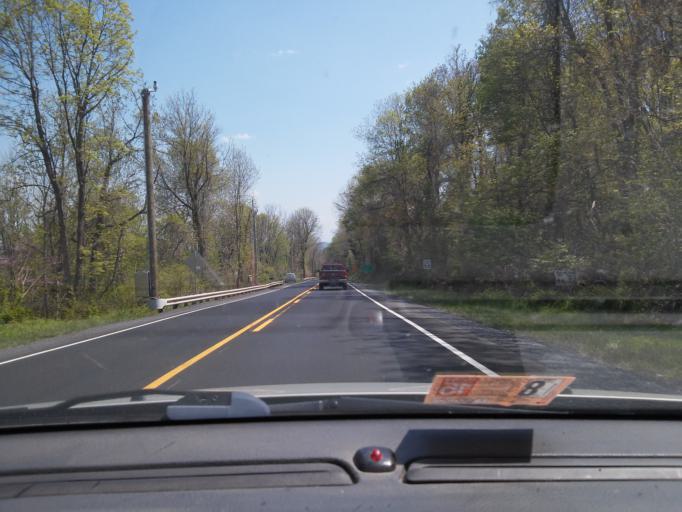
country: US
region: Virginia
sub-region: Warren County
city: Apple Mountain Lake
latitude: 38.8601
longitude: -78.1304
